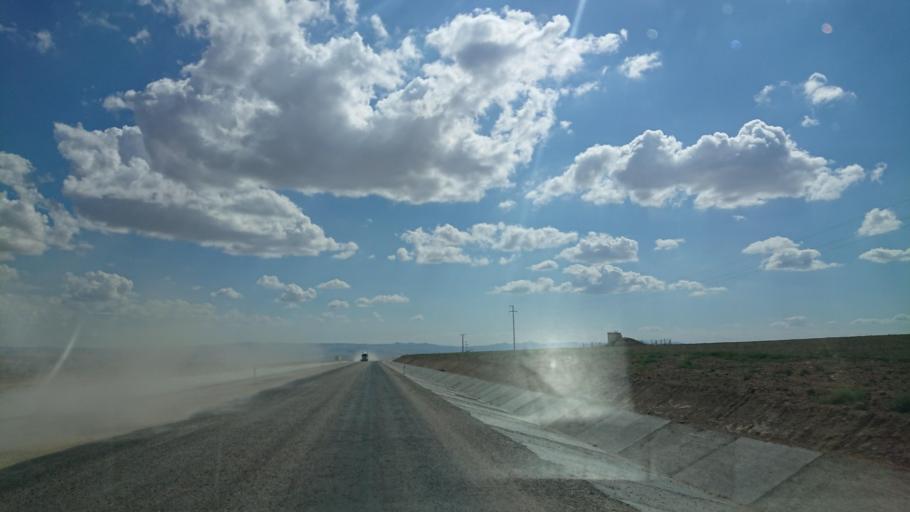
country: TR
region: Kirsehir
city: Kirsehir
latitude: 39.1293
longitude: 34.0376
